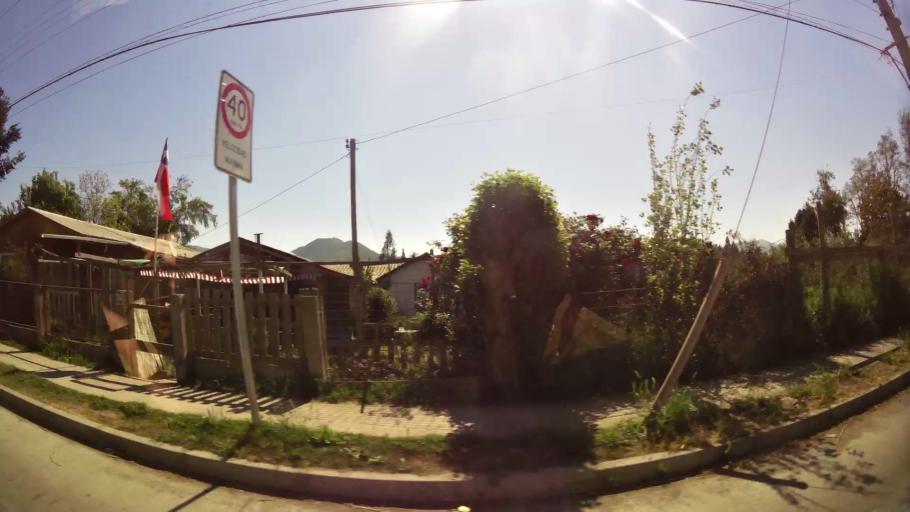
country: CL
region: Santiago Metropolitan
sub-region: Provincia de Talagante
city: Penaflor
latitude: -33.5960
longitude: -70.8811
